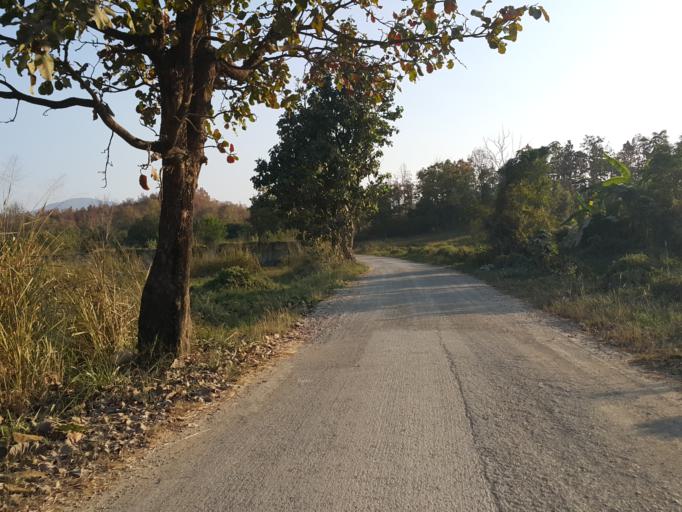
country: TH
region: Chiang Mai
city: Mae On
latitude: 18.8018
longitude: 99.2505
